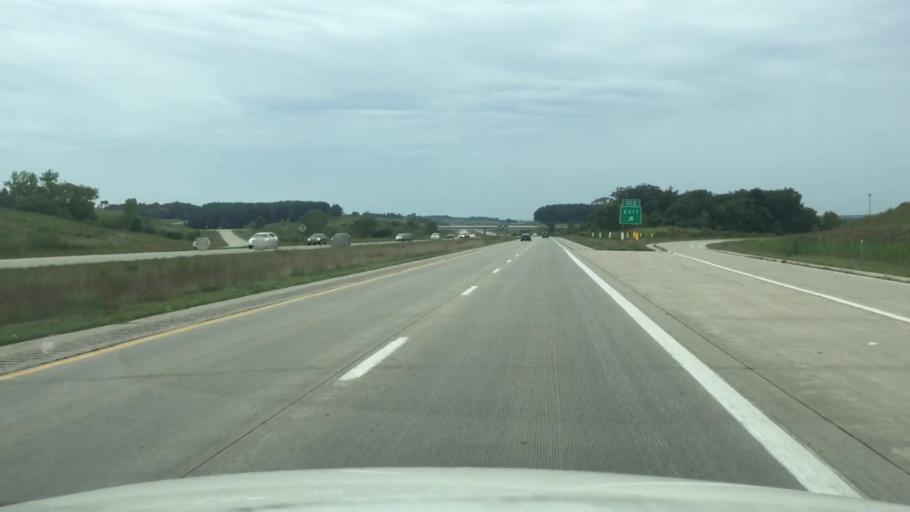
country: US
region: Iowa
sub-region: Polk County
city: West Des Moines
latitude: 41.5228
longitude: -93.7401
